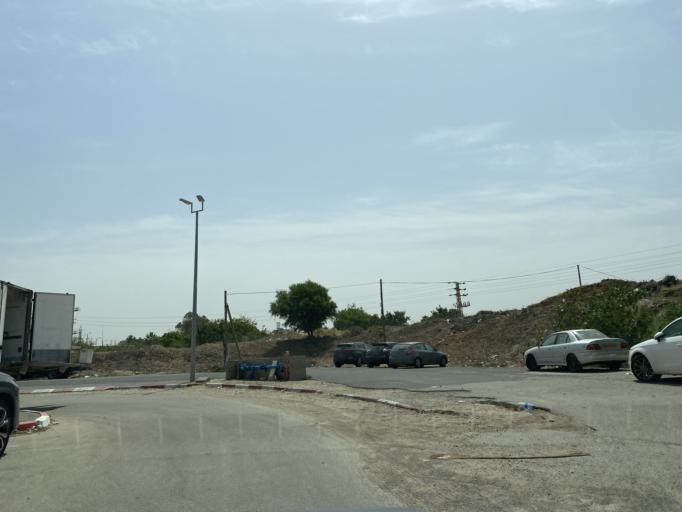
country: IL
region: Tel Aviv
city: Herzliyya
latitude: 32.1573
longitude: 34.8099
